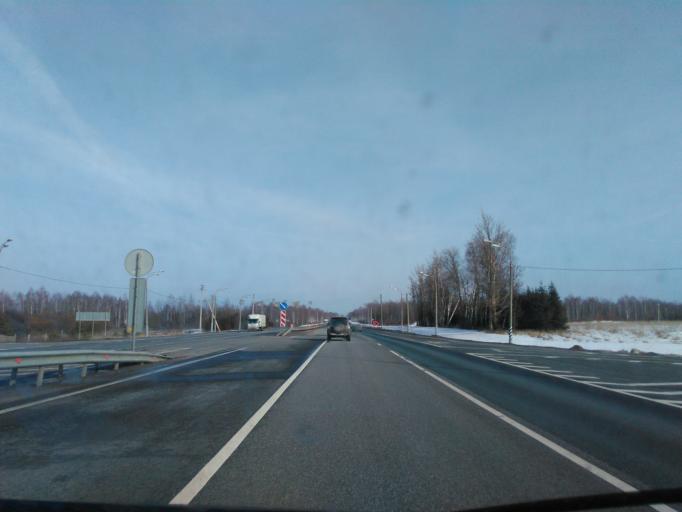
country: RU
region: Smolensk
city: Verkhnedneprovskiy
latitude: 55.1818
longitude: 33.5654
